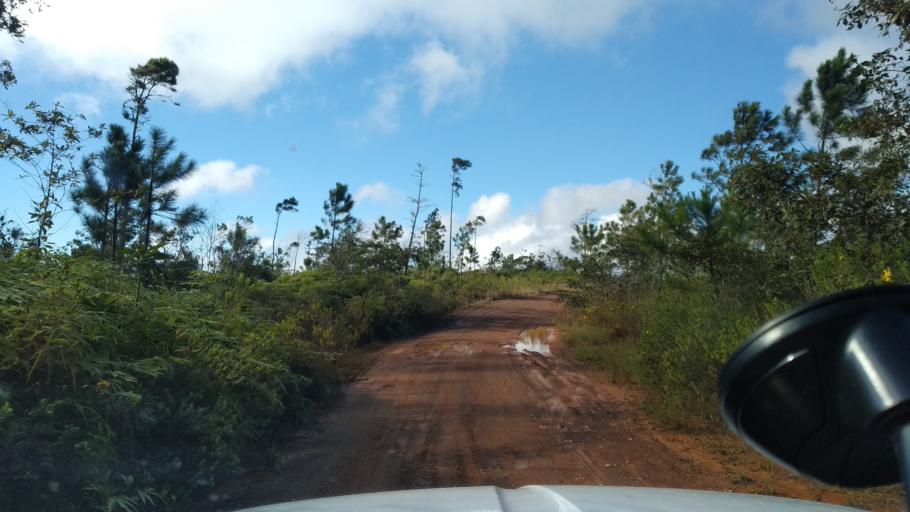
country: BZ
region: Cayo
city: Belmopan
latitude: 16.9955
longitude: -88.8276
